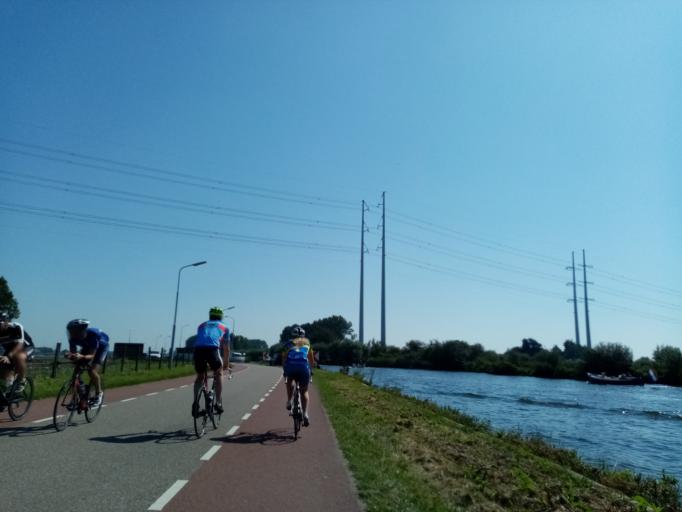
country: NL
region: South Holland
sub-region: Gemeente Kaag en Braassem
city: Oude Wetering
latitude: 52.2152
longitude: 4.6014
